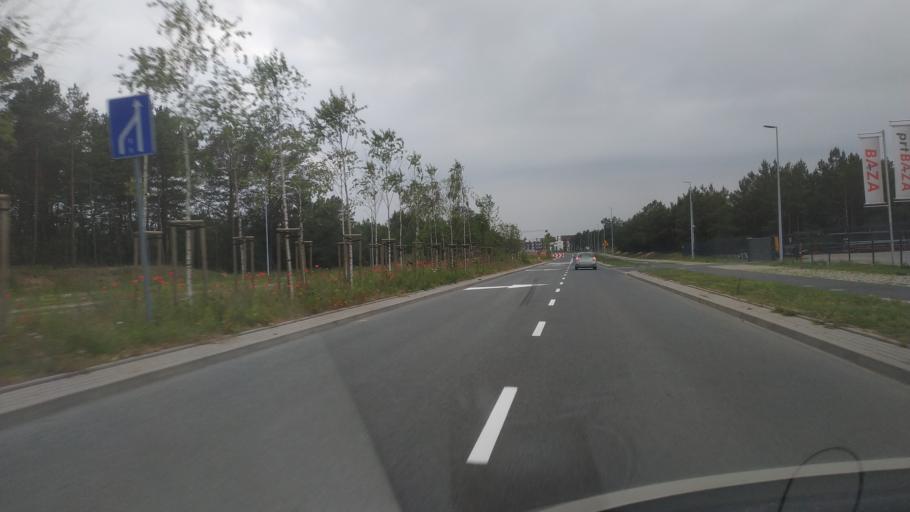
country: PL
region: Kujawsko-Pomorskie
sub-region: Powiat torunski
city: Lysomice
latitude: 53.0523
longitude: 18.6138
